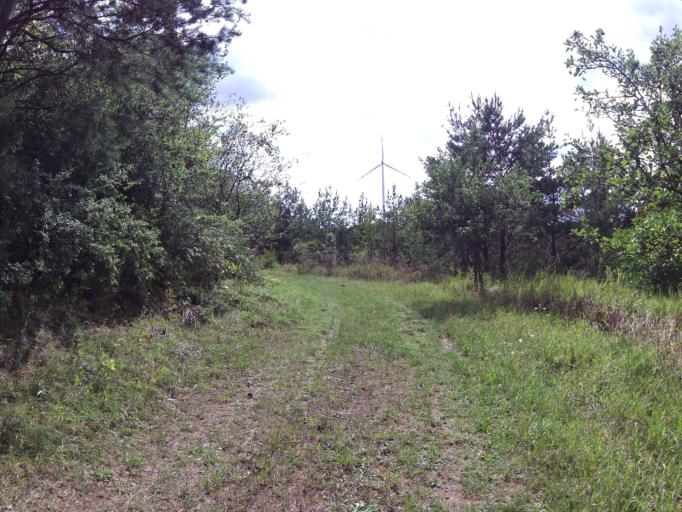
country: DE
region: Bavaria
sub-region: Regierungsbezirk Unterfranken
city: Margetshochheim
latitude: 49.8377
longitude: 9.8423
